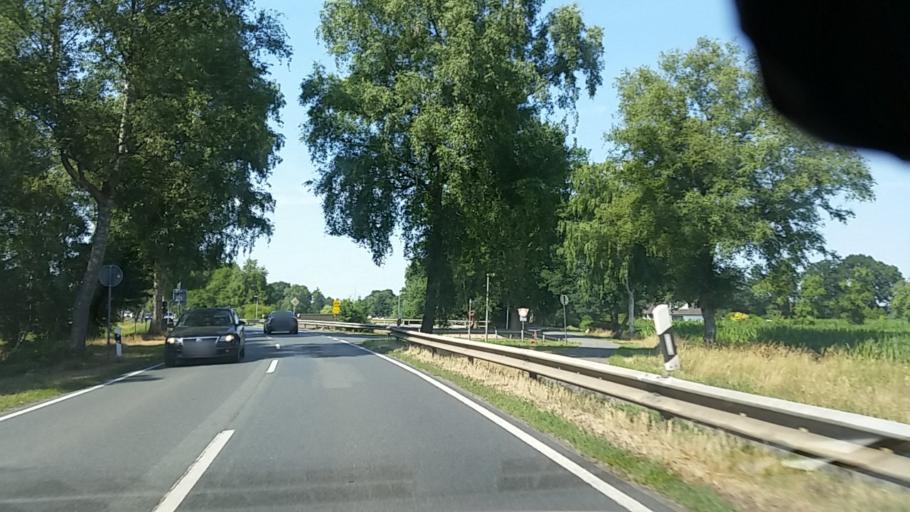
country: DE
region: Lower Saxony
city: Ottersberg
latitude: 53.0659
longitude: 9.1714
